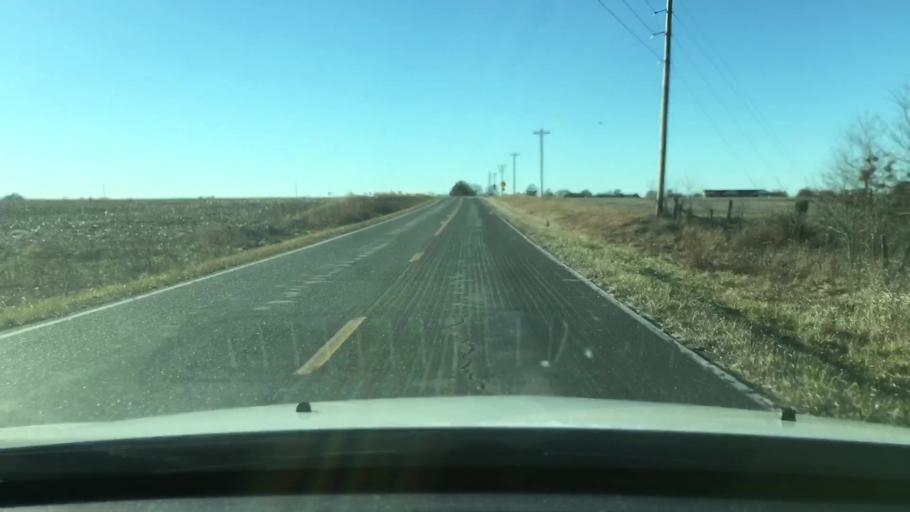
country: US
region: Missouri
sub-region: Audrain County
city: Mexico
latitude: 39.2761
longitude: -91.8093
